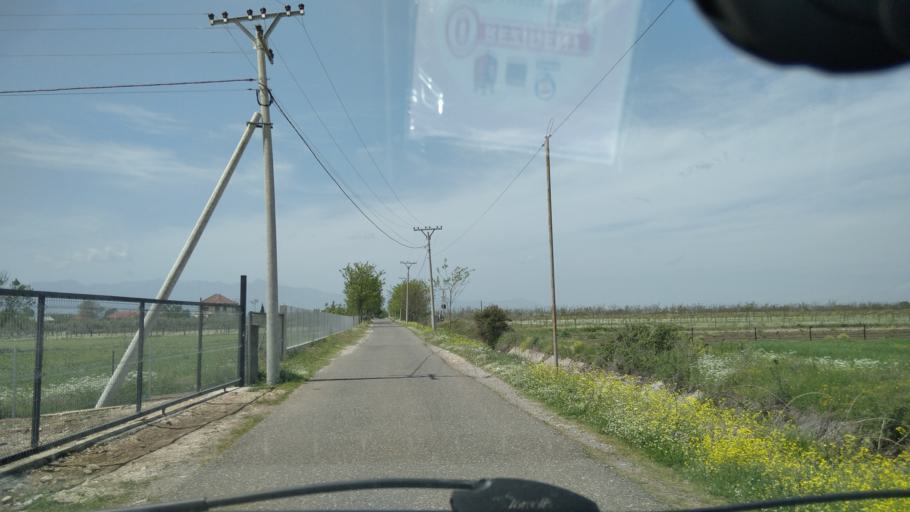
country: AL
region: Shkoder
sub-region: Rrethi i Malesia e Madhe
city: Gruemire
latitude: 42.1424
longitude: 19.5198
